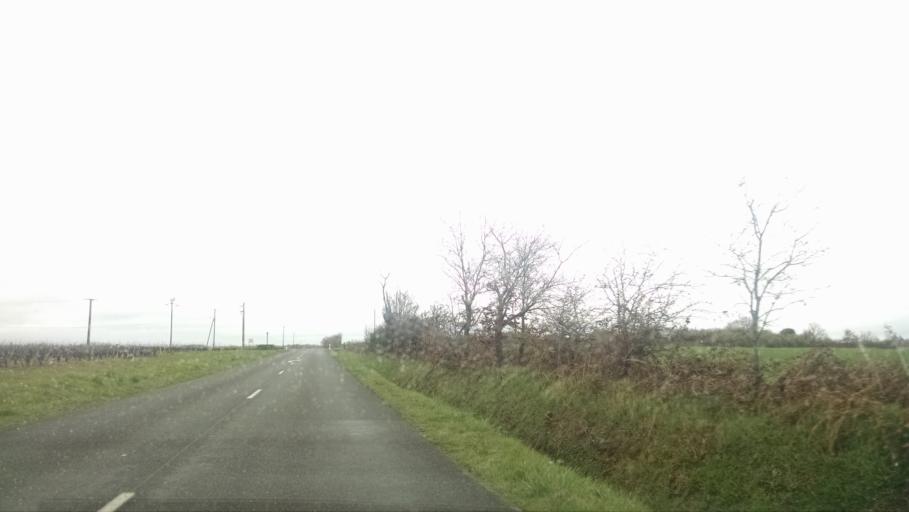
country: FR
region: Pays de la Loire
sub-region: Departement de la Loire-Atlantique
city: Maisdon-sur-Sevre
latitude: 47.0847
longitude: -1.3883
